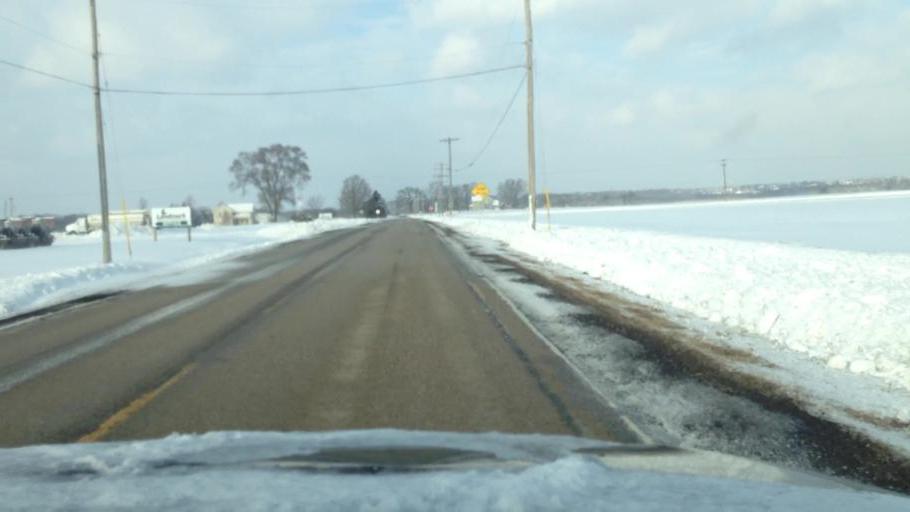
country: US
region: Wisconsin
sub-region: Walworth County
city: East Troy
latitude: 42.7905
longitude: -88.4449
